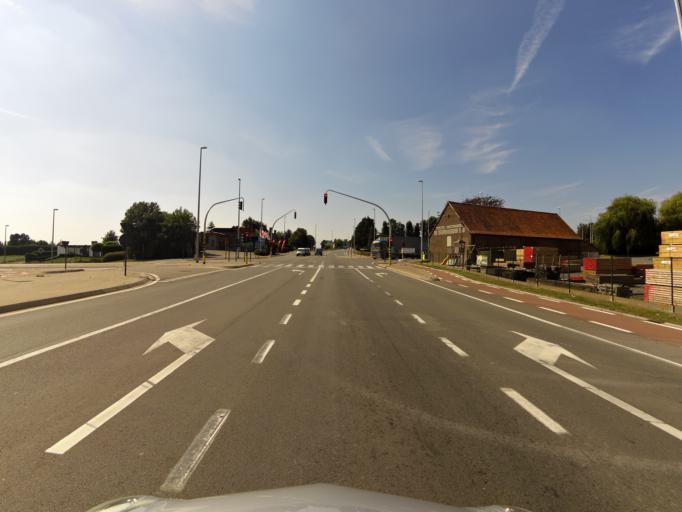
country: BE
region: Flanders
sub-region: Provincie West-Vlaanderen
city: Tielt
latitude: 50.9974
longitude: 3.3500
